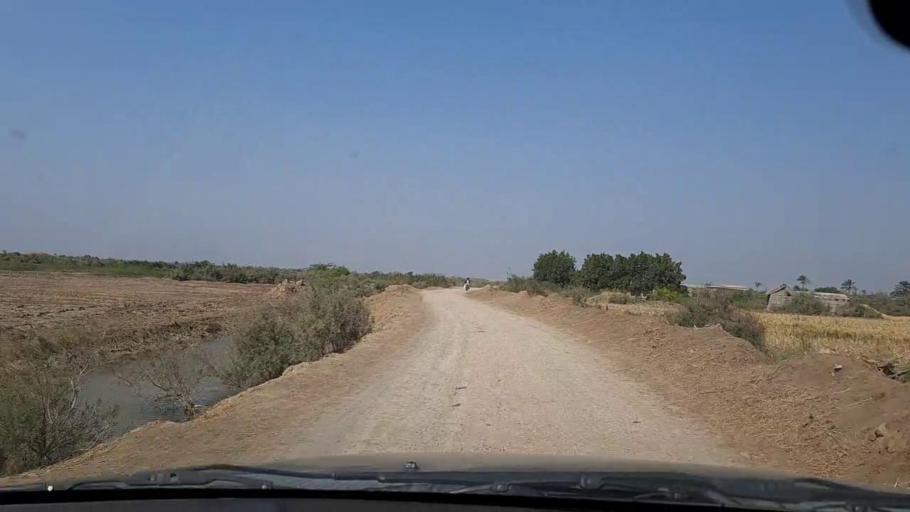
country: PK
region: Sindh
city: Mirpur Sakro
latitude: 24.3587
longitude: 67.6831
